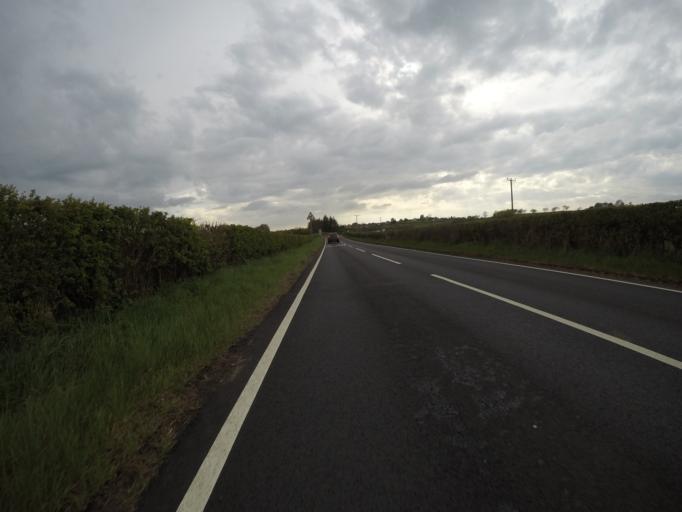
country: GB
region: Scotland
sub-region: East Ayrshire
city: Kilmaurs
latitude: 55.6422
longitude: -4.5143
